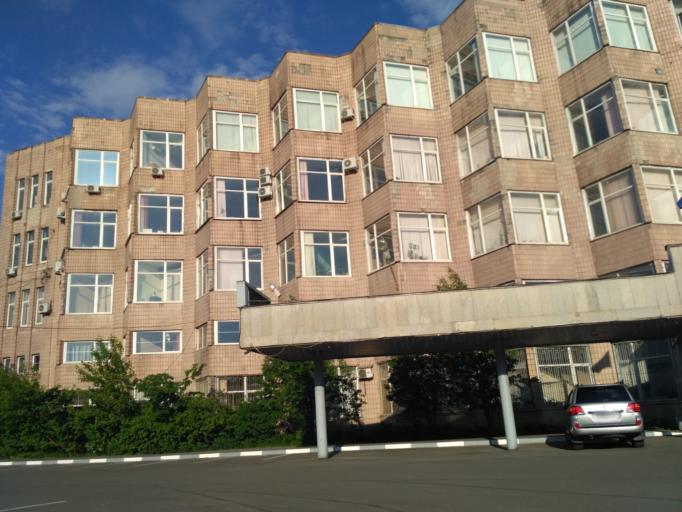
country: RU
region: Leningrad
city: Kalininskiy
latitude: 59.9950
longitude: 30.3803
